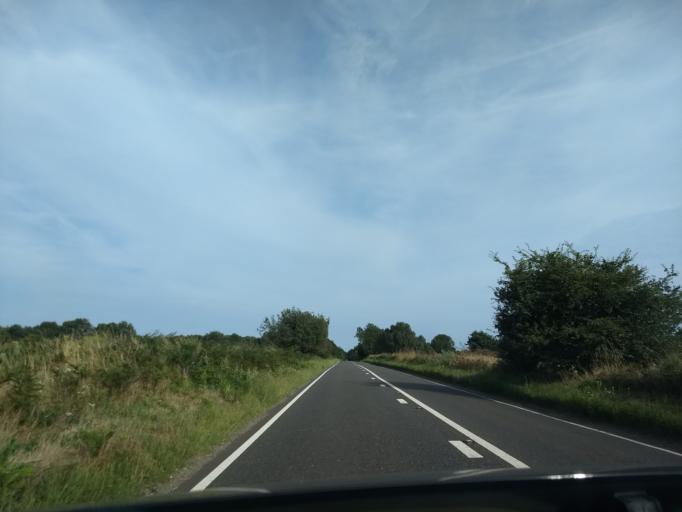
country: GB
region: England
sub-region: Suffolk
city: Woodbridge
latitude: 52.0858
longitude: 1.3701
